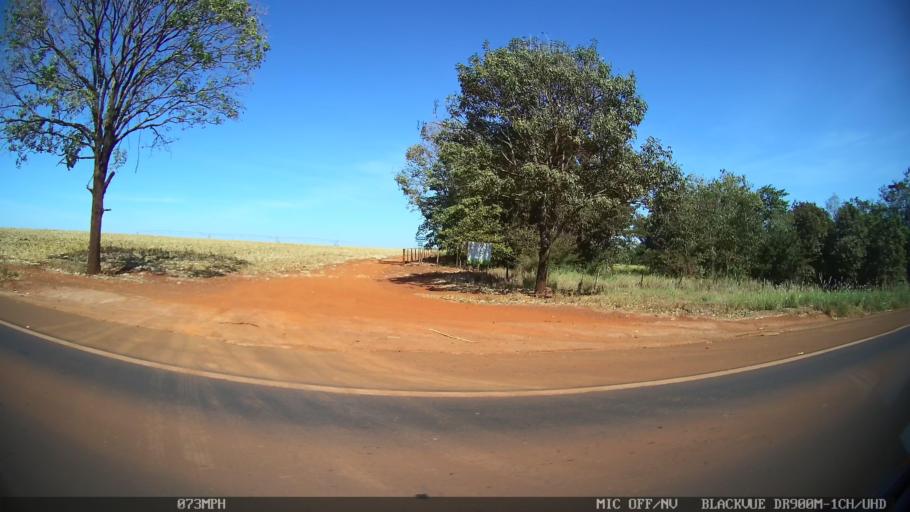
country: BR
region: Sao Paulo
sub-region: Guaira
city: Guaira
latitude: -20.4443
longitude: -48.3622
